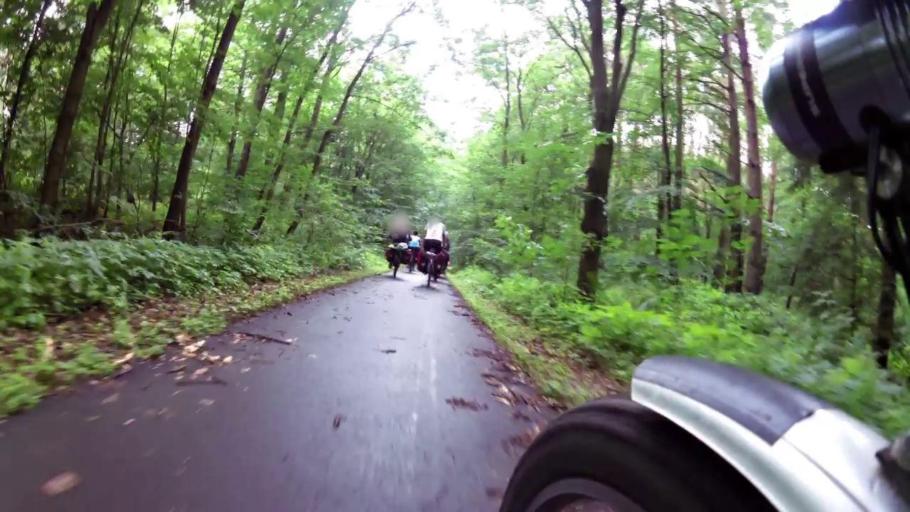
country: PL
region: West Pomeranian Voivodeship
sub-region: Powiat gryfinski
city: Banie
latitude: 53.0531
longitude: 14.6281
